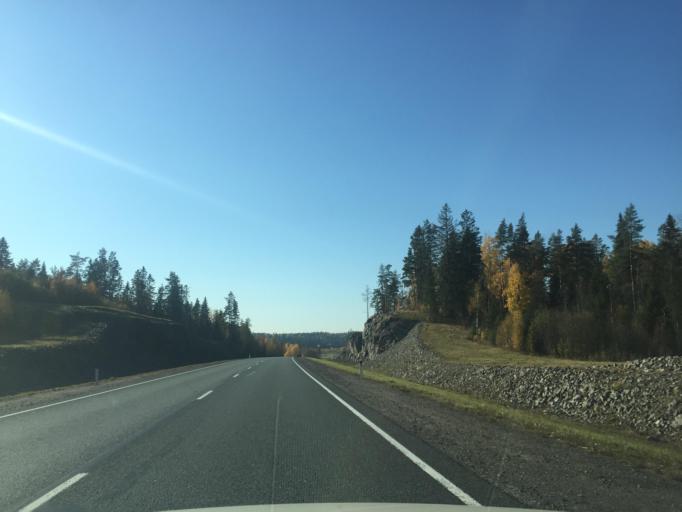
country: RU
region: Leningrad
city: Kuznechnoye
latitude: 61.3450
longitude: 29.8734
